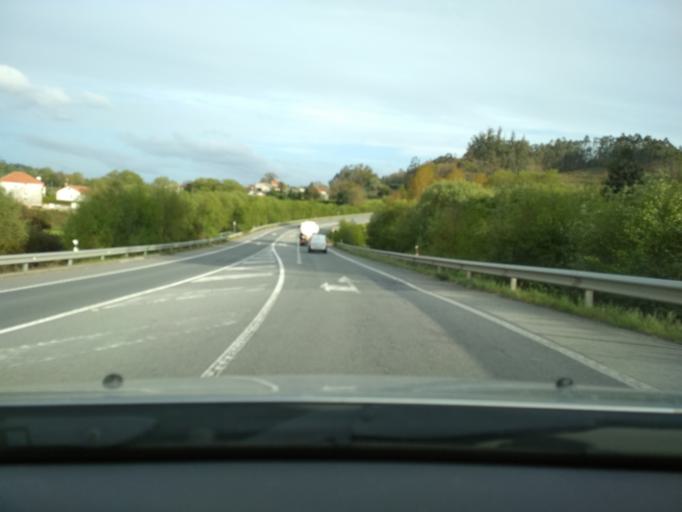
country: ES
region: Galicia
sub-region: Provincia da Coruna
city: Cerceda
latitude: 43.2191
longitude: -8.4575
